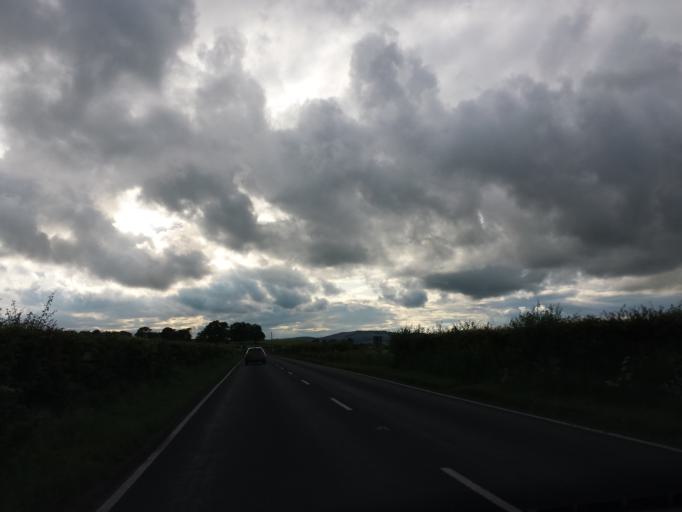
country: GB
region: Scotland
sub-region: Fife
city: Strathkinness
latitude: 56.3527
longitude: -2.8483
